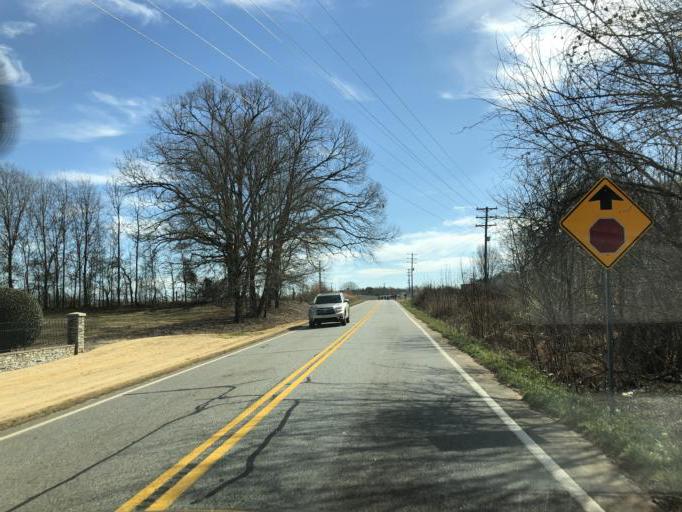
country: US
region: South Carolina
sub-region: Spartanburg County
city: Boiling Springs
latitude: 35.0516
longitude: -81.9285
